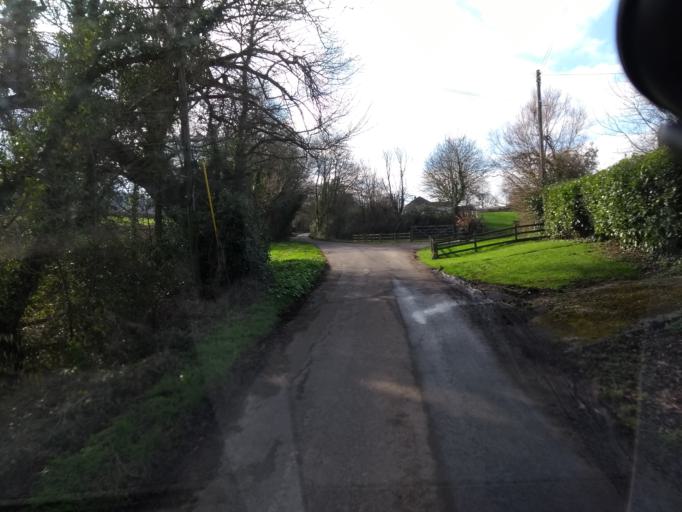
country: GB
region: England
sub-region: Somerset
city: Creech Saint Michael
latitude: 50.9542
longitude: -3.0322
